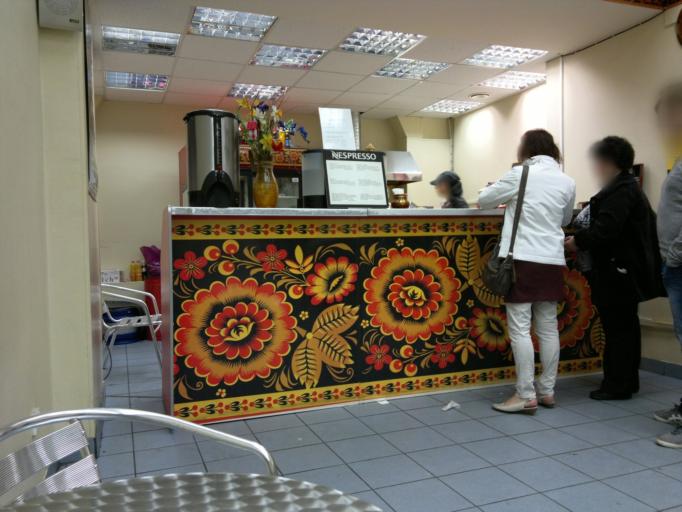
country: RU
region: St.-Petersburg
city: Saint Petersburg
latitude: 59.9333
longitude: 30.3324
